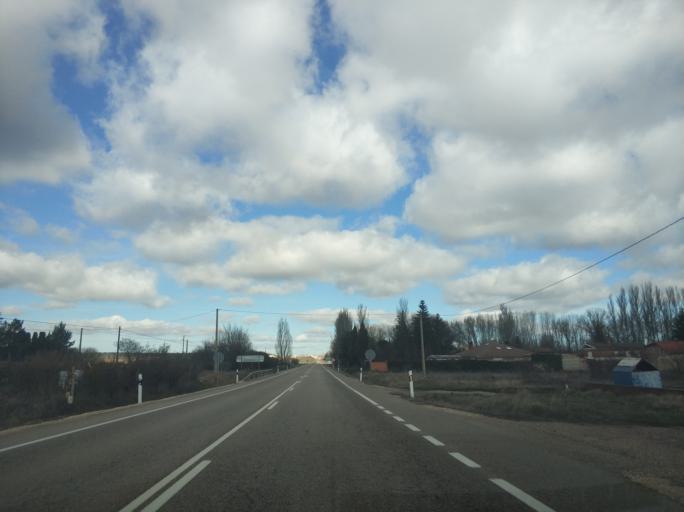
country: ES
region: Castille and Leon
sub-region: Provincia de Burgos
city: Revillarruz
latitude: 42.2316
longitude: -3.6632
